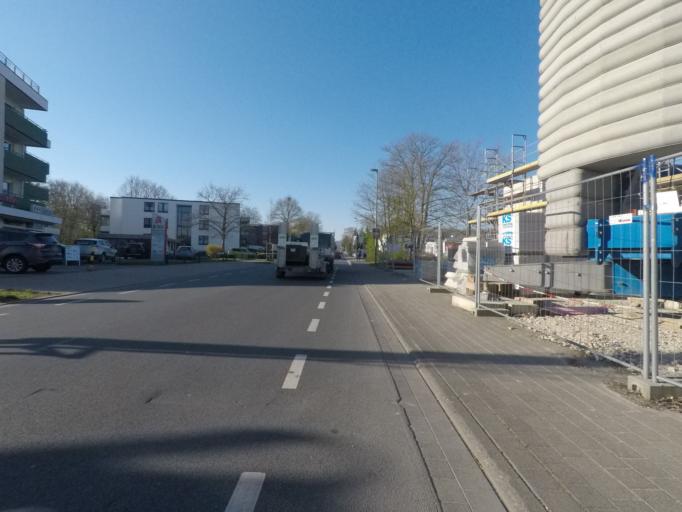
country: DE
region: North Rhine-Westphalia
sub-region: Regierungsbezirk Detmold
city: Bielefeld
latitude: 52.0278
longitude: 8.6032
